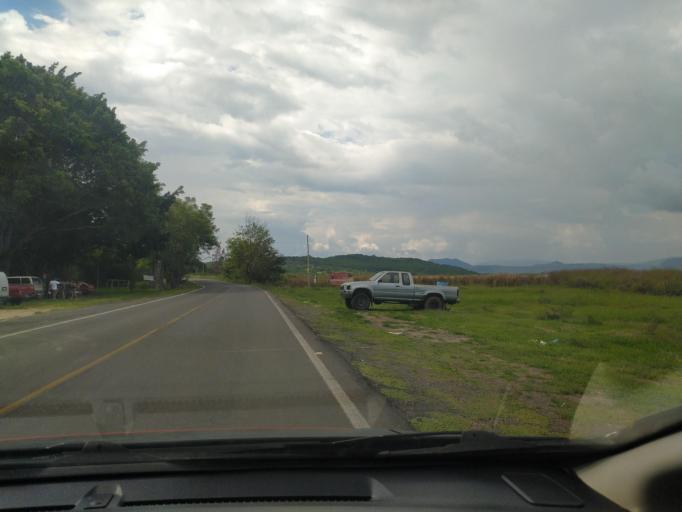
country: MX
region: Jalisco
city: Villa Corona
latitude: 20.3565
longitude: -103.6663
